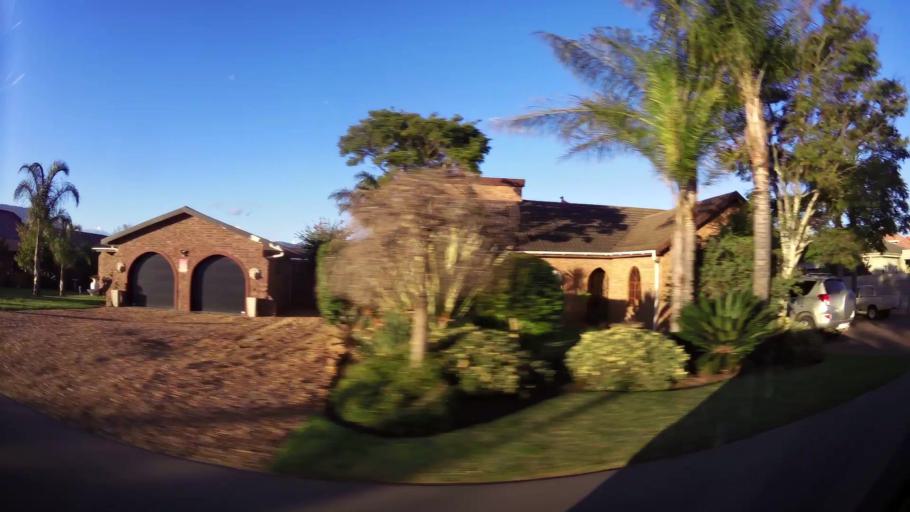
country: ZA
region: Western Cape
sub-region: Eden District Municipality
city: Riversdale
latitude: -34.0830
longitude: 21.2420
